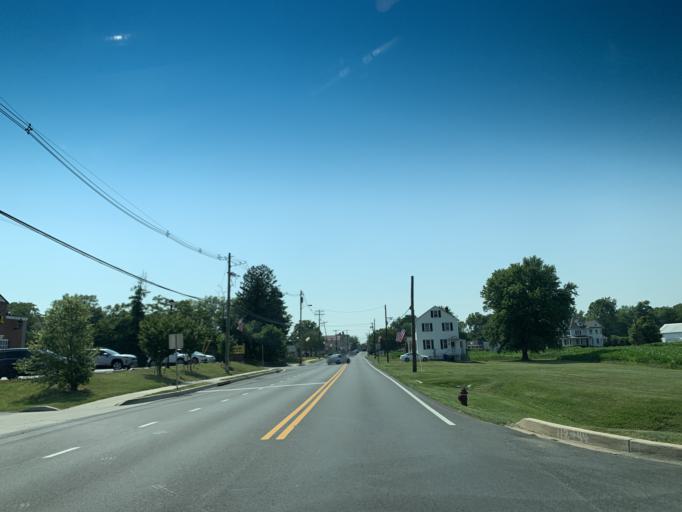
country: US
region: Maryland
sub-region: Montgomery County
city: Poolesville
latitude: 39.1450
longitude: -77.4127
